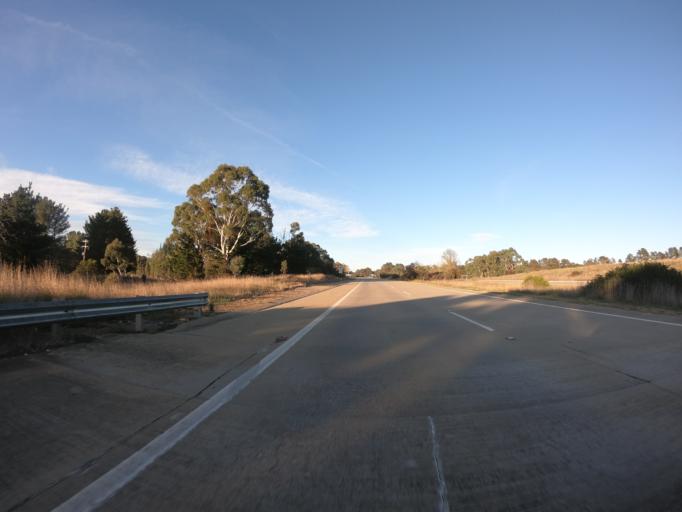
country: AU
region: New South Wales
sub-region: Yass Valley
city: Gundaroo
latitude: -35.1414
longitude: 149.3357
